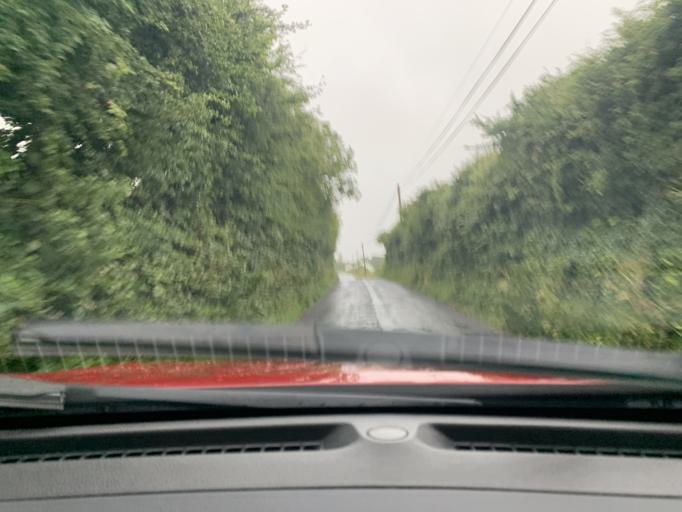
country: IE
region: Connaught
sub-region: County Leitrim
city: Kinlough
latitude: 54.4429
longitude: -8.4401
